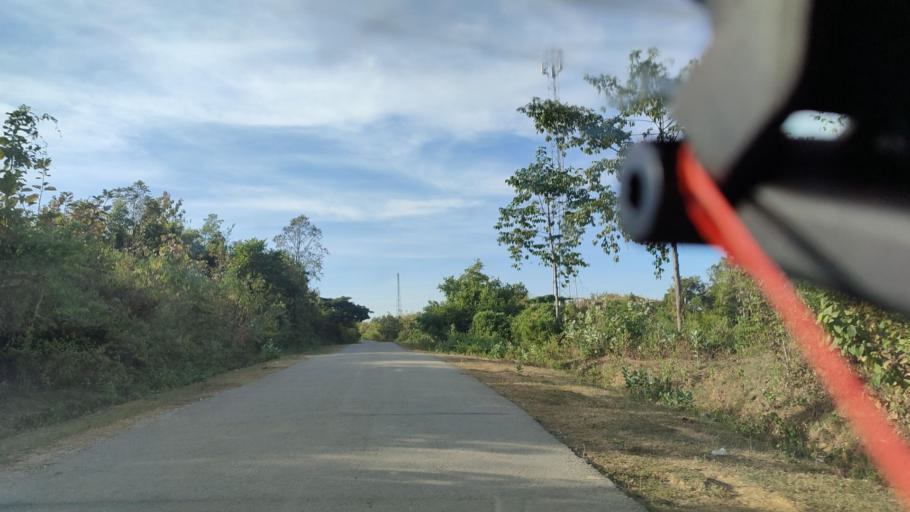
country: MM
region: Magway
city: Taungdwingyi
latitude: 20.0103
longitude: 95.8417
